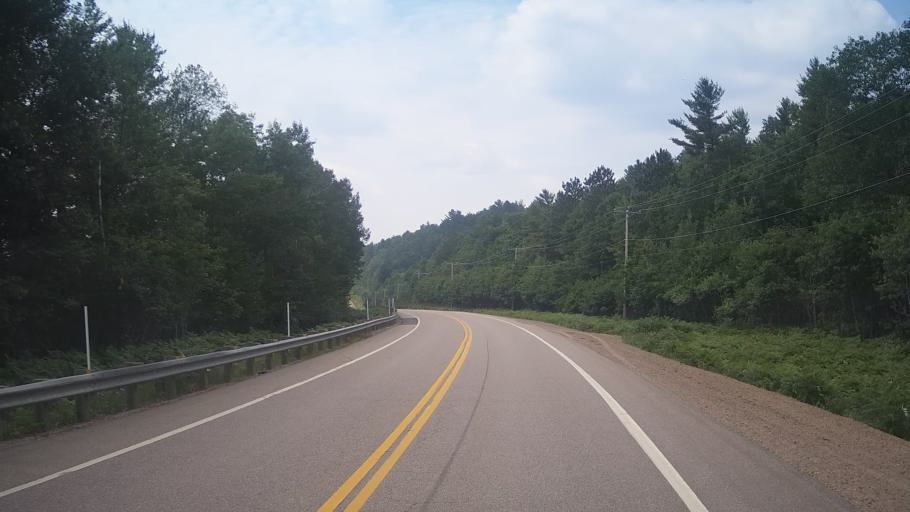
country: CA
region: Quebec
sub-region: Outaouais
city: Fort-Coulonge
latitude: 45.9170
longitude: -76.9287
